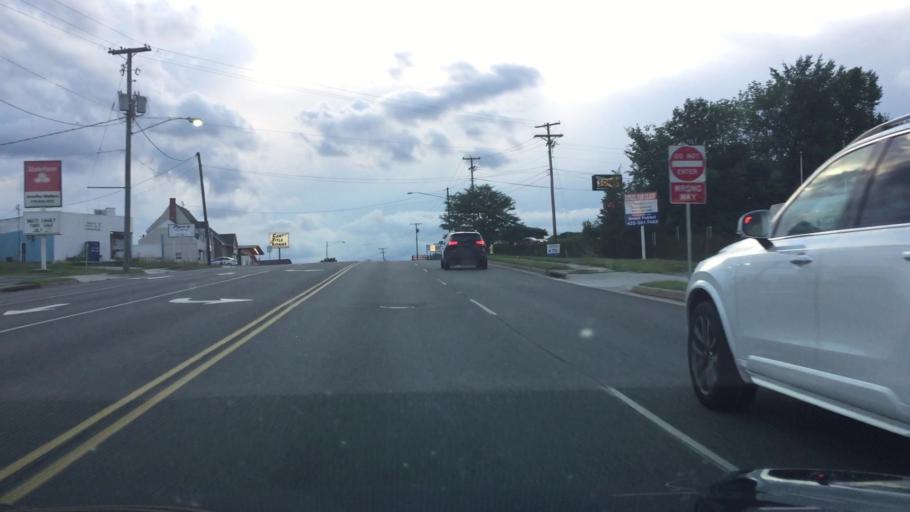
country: US
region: Virginia
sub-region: Wythe County
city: Wytheville
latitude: 36.9531
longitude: -81.0751
